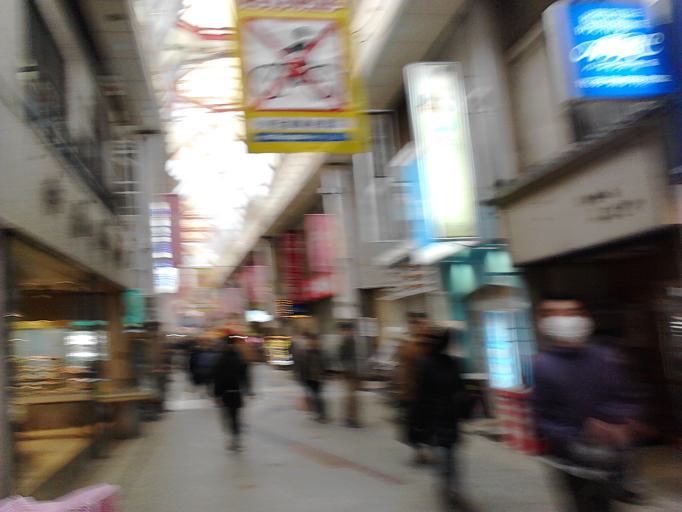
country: JP
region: Tokyo
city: Tokyo
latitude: 35.7028
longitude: 139.6367
